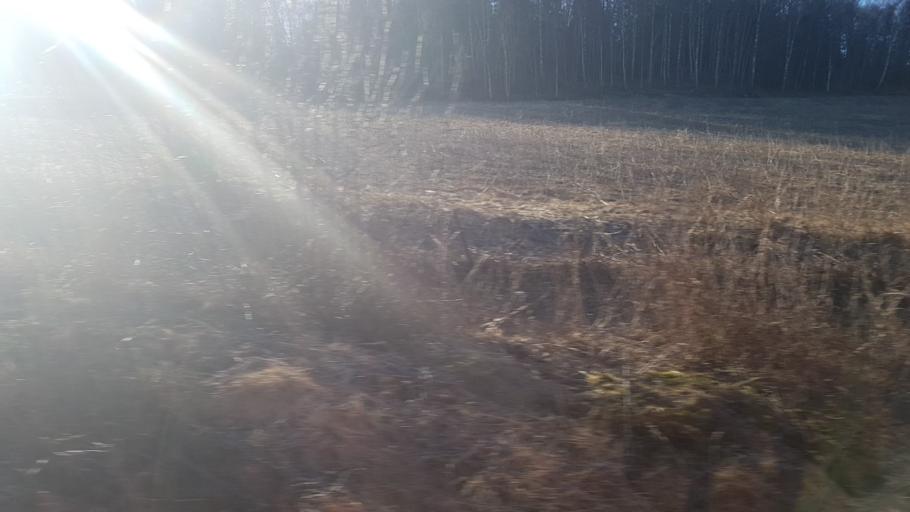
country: NO
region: Nord-Trondelag
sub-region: Levanger
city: Skogn
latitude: 63.7200
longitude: 11.2437
